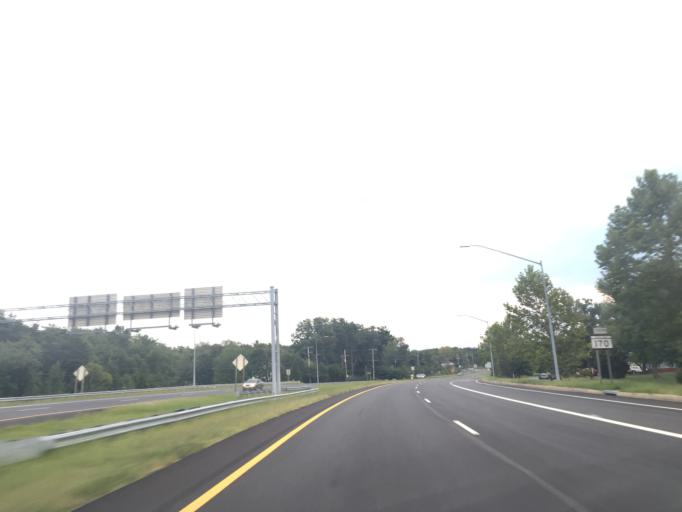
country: US
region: Maryland
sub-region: Anne Arundel County
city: Severn
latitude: 39.1477
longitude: -76.6866
